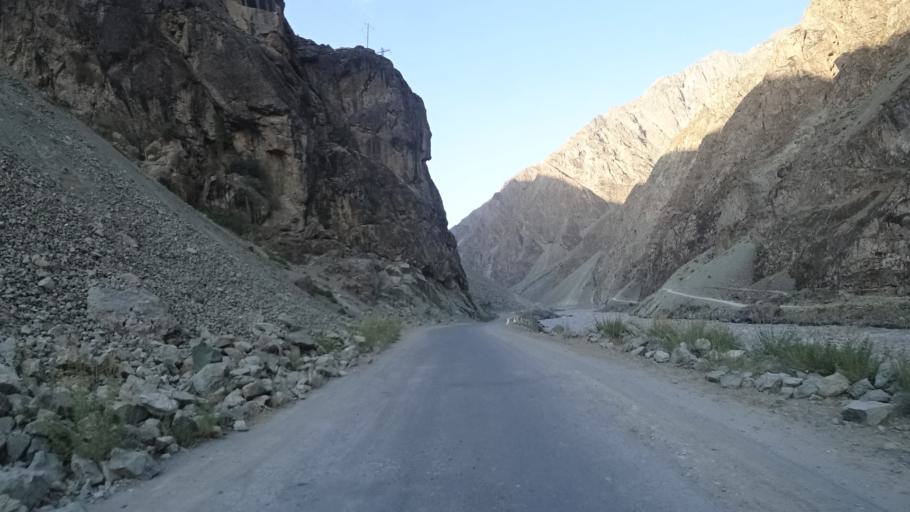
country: TJ
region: Gorno-Badakhshan
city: Qalaikhumb
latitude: 38.4226
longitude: 70.7443
